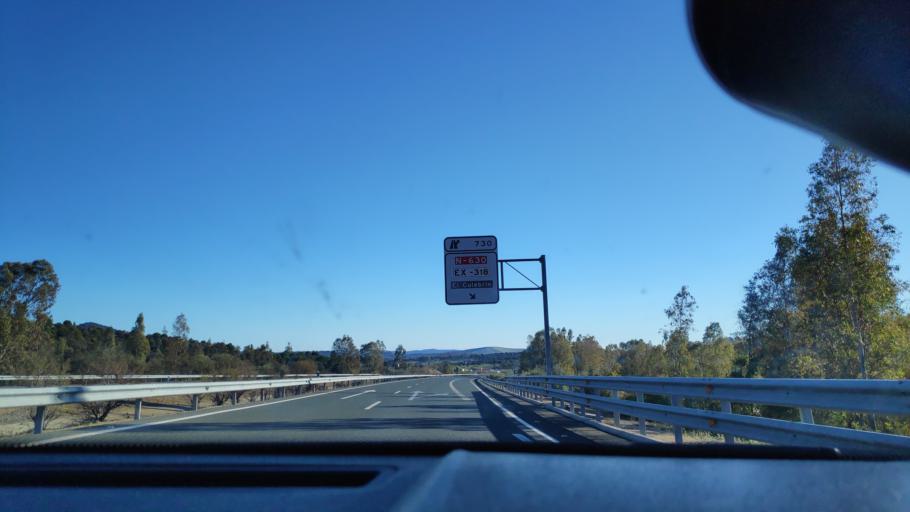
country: ES
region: Extremadura
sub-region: Provincia de Badajoz
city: Monesterio
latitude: 38.0360
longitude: -6.2244
